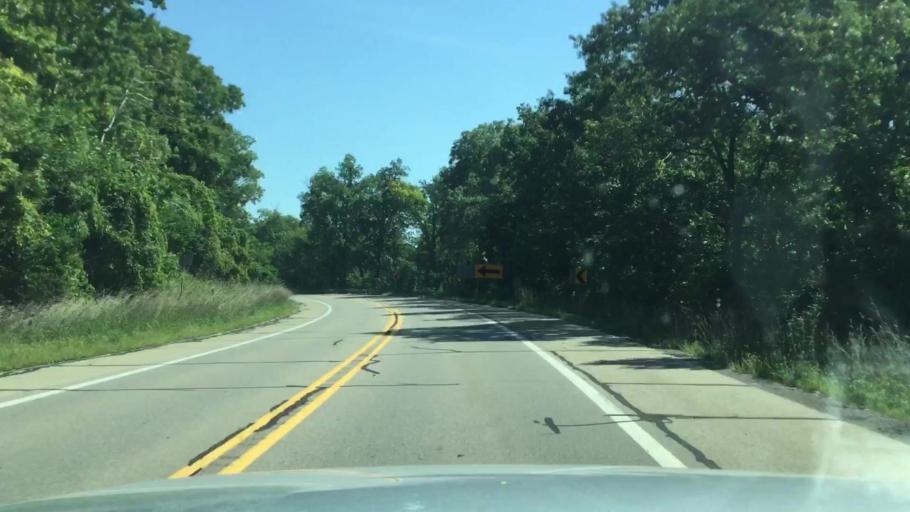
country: US
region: Michigan
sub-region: Jackson County
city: Brooklyn
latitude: 42.0615
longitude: -84.1884
